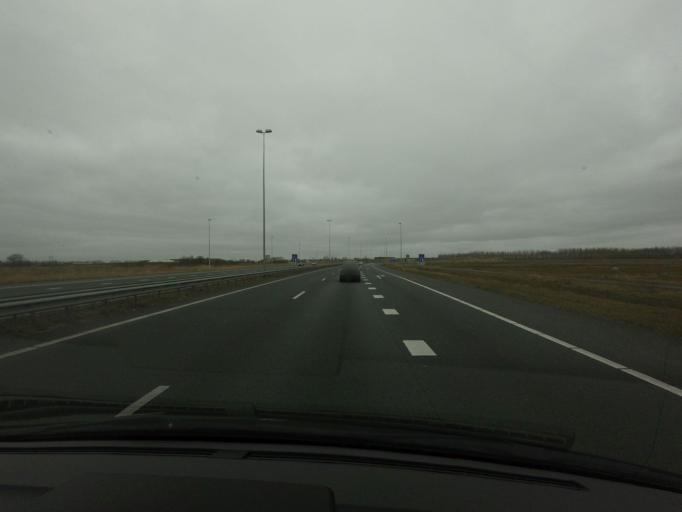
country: NL
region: Groningen
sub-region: Gemeente Haren
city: Haren
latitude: 53.2024
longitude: 6.6360
